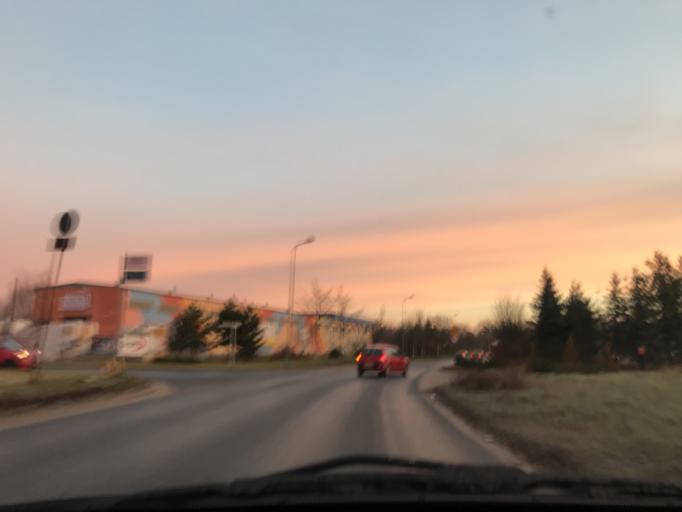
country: PL
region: Greater Poland Voivodeship
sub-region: Powiat poznanski
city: Baranowo
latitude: 52.4273
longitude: 16.7982
